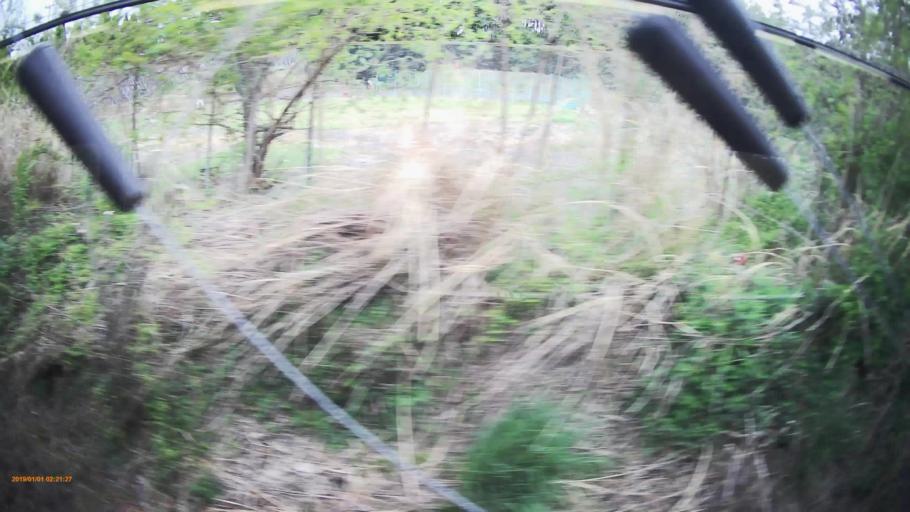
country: JP
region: Yamanashi
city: Ryuo
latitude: 35.6785
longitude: 138.4994
